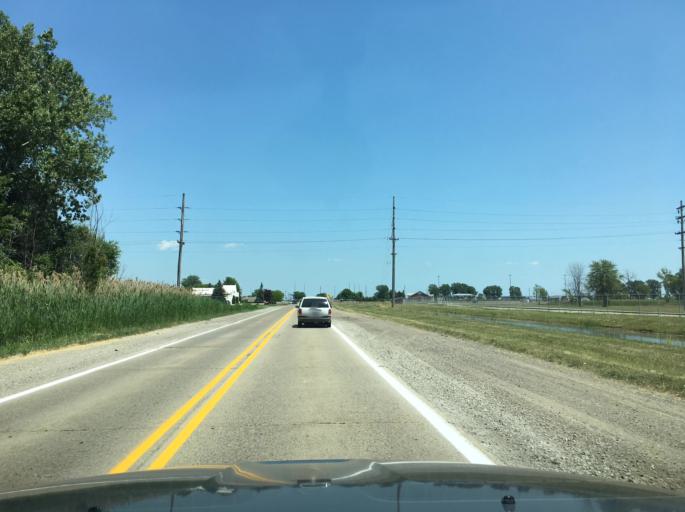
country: US
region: Michigan
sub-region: Macomb County
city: Mount Clemens
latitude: 42.6306
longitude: -82.8297
